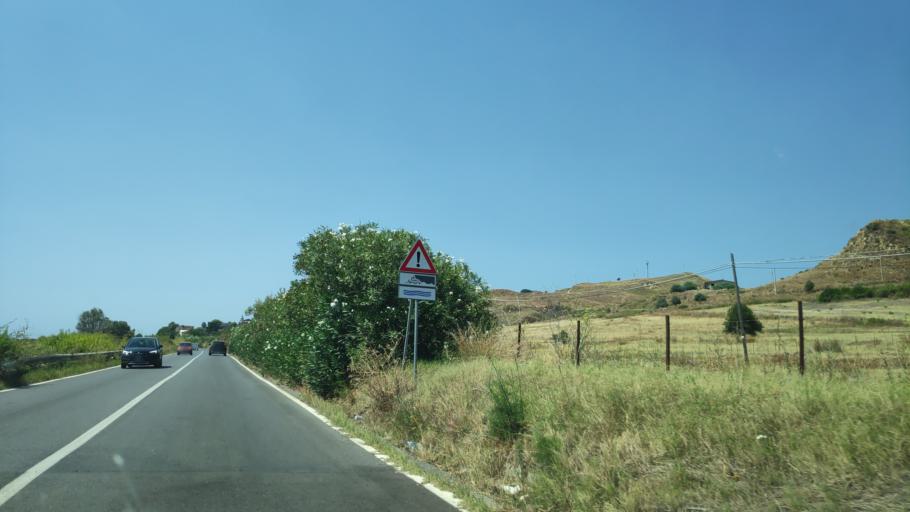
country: IT
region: Calabria
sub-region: Provincia di Reggio Calabria
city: Weather Station
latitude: 37.9427
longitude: 16.0812
